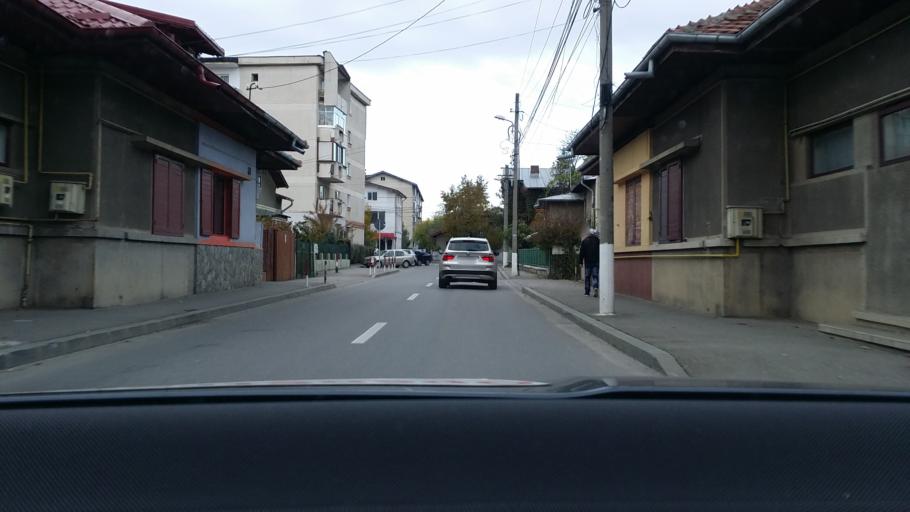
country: RO
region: Prahova
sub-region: Municipiul Campina
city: Campina
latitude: 45.1234
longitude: 25.7394
